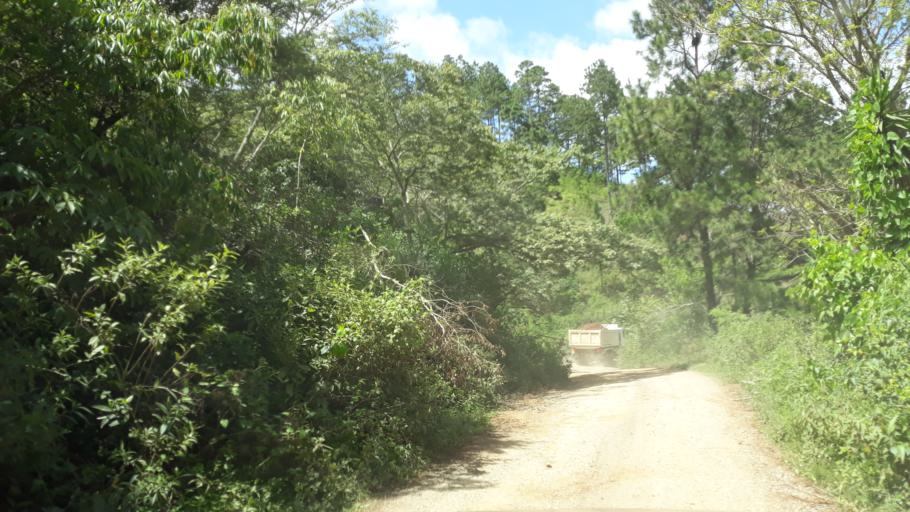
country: HN
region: El Paraiso
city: Santa Cruz
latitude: 13.7539
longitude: -86.6581
